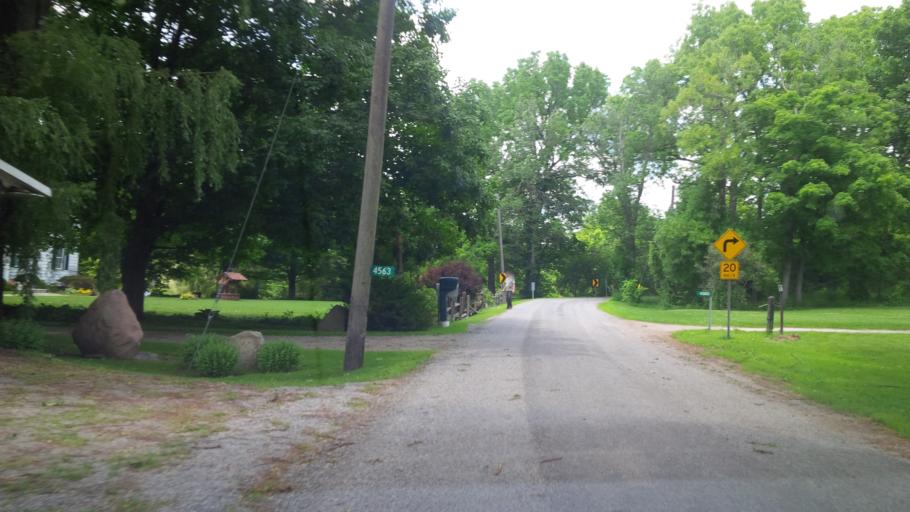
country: CA
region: Ontario
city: Burlington
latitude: 43.4398
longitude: -79.8702
